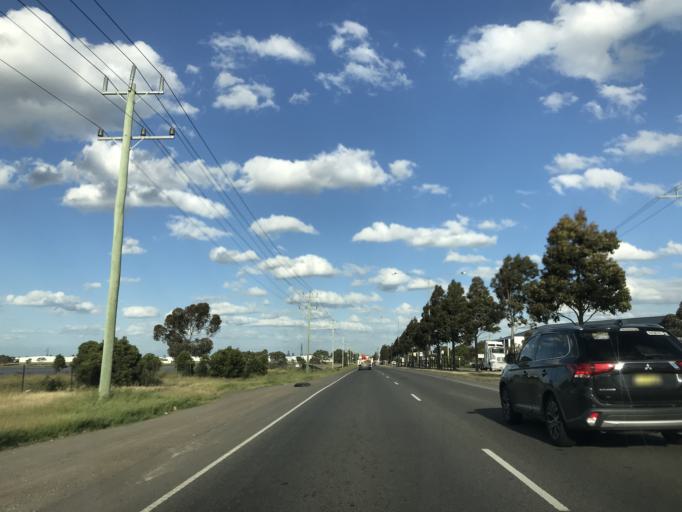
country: AU
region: Victoria
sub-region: Brimbank
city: Derrimut
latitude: -37.8136
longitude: 144.7895
